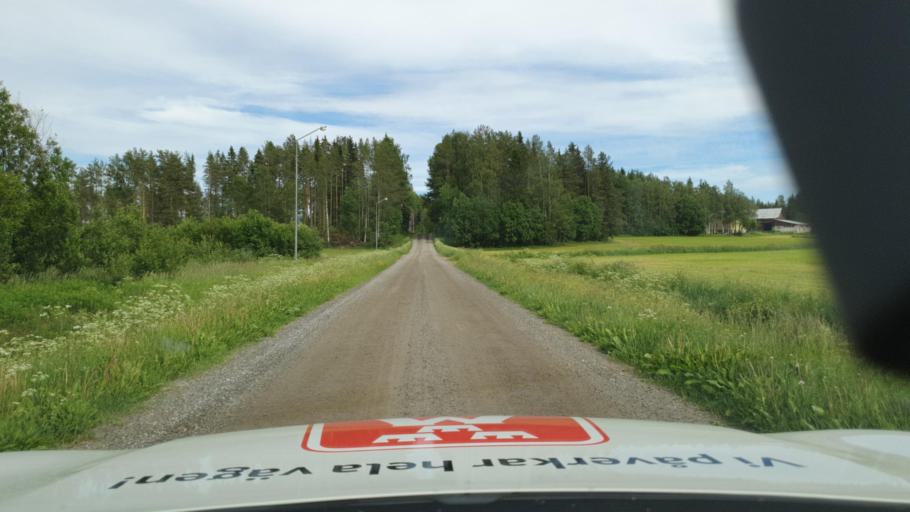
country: SE
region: Vaesterbotten
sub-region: Robertsfors Kommun
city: Robertsfors
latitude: 64.3731
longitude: 21.0470
